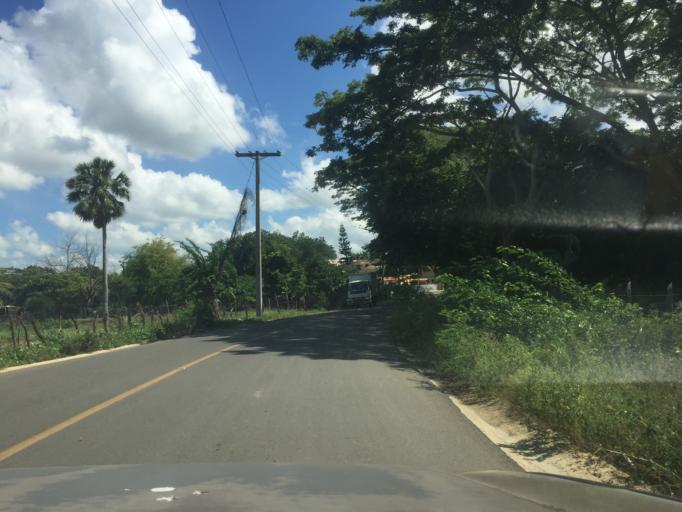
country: DO
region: Santiago
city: Santiago de los Caballeros
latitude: 19.4452
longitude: -70.7566
